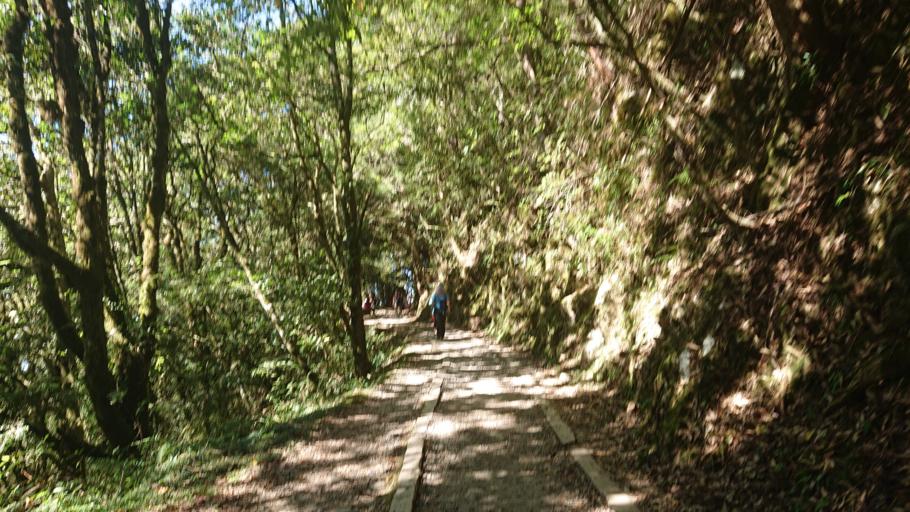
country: TW
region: Taiwan
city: Lugu
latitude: 23.4802
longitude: 120.8250
